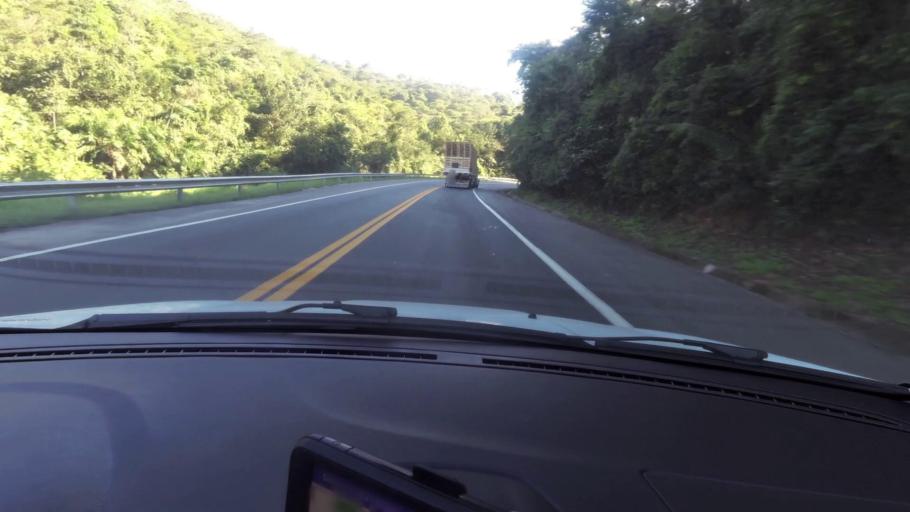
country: BR
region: Espirito Santo
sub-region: Alfredo Chaves
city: Alfredo Chaves
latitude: -20.6651
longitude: -40.6544
